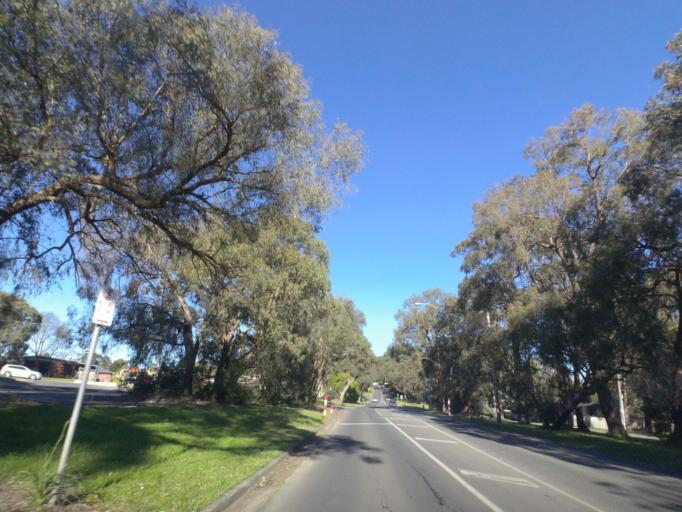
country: AU
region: Victoria
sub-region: Yarra Ranges
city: Kilsyth
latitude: -37.7981
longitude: 145.3266
